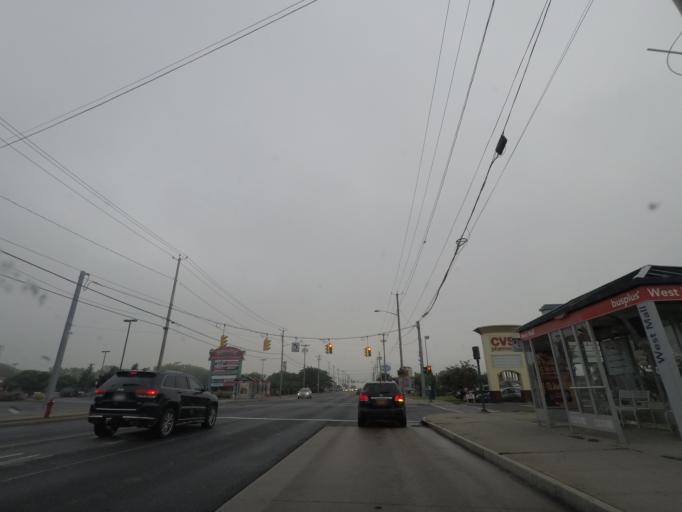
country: US
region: New York
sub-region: Albany County
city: West Albany
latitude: 42.6801
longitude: -73.7900
